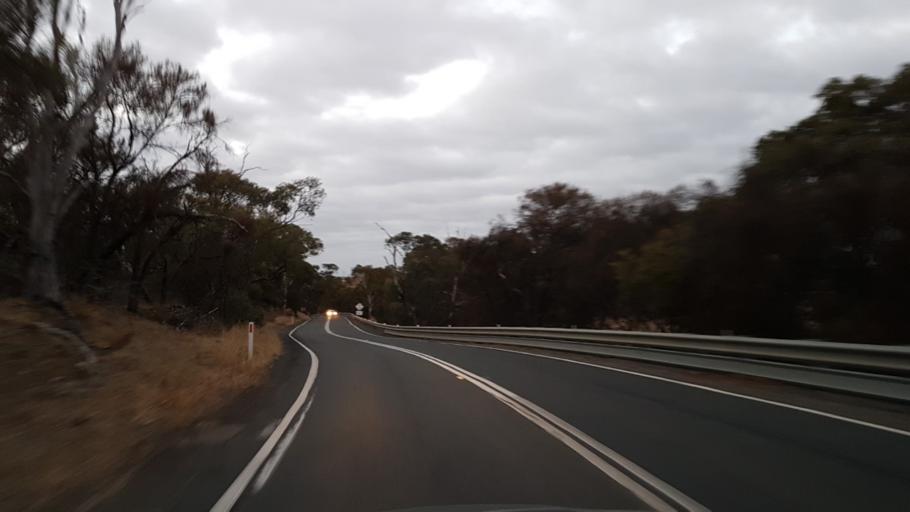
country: AU
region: South Australia
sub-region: Mount Barker
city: Callington
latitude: -35.0501
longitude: 139.0008
